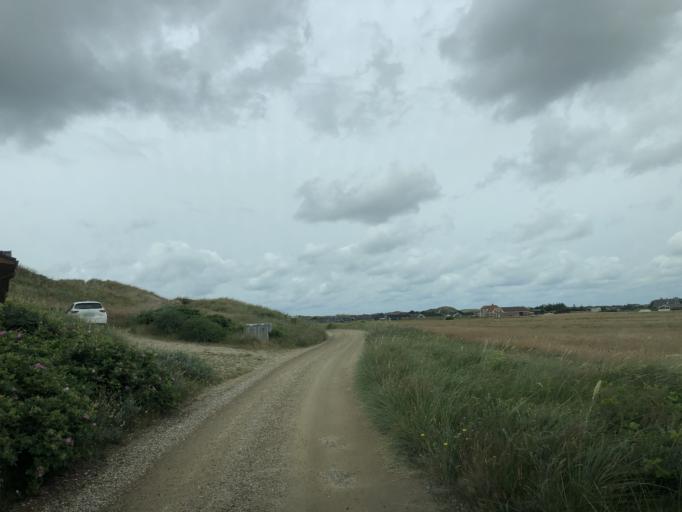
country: DK
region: Central Jutland
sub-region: Ringkobing-Skjern Kommune
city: Hvide Sande
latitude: 55.9241
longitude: 8.1671
